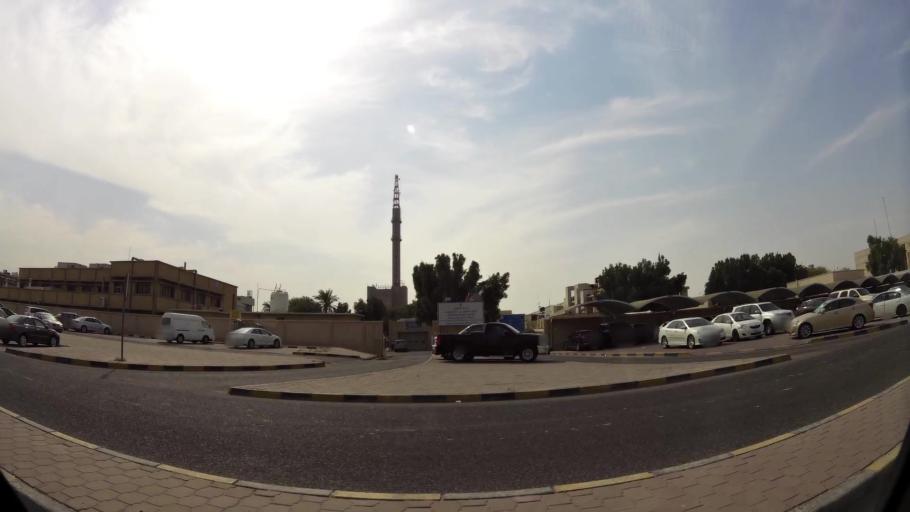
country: KW
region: Al Asimah
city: Ash Shamiyah
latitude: 29.3423
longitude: 47.9508
